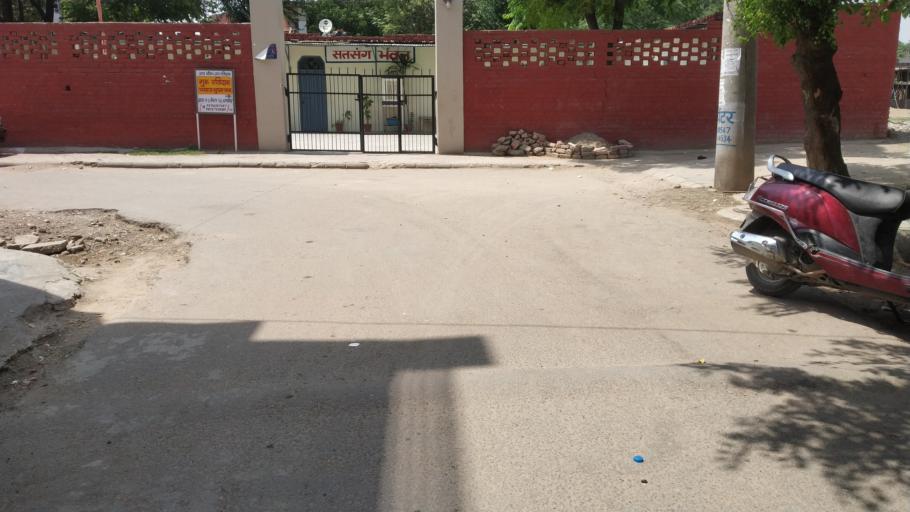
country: IN
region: Punjab
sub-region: Ajitgarh
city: Mohali
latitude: 30.7126
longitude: 76.7329
